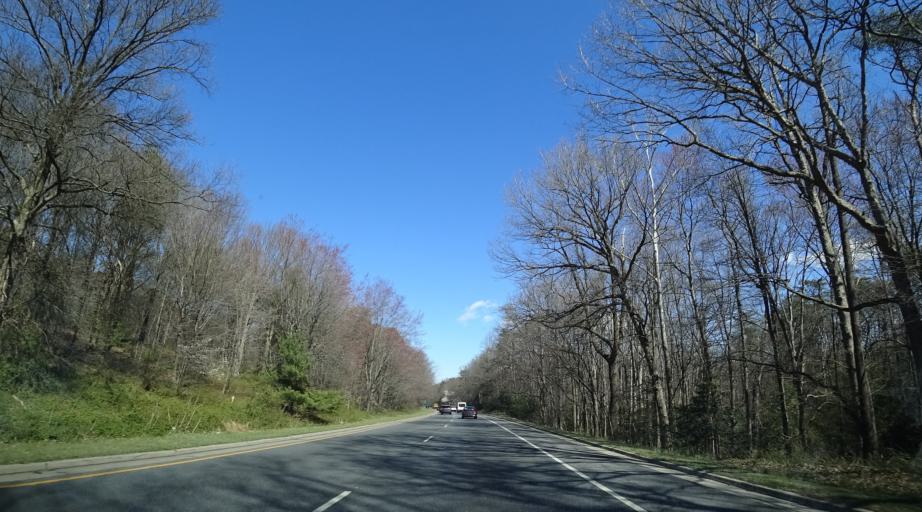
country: US
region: Maryland
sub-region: Prince George's County
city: New Carrollton
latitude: 38.9782
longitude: -76.8940
